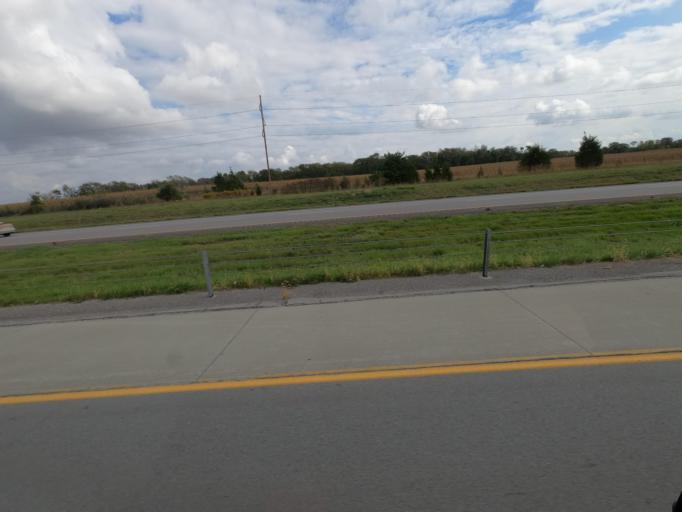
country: US
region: Iowa
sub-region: Story County
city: Huxley
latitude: 41.9481
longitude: -93.5699
